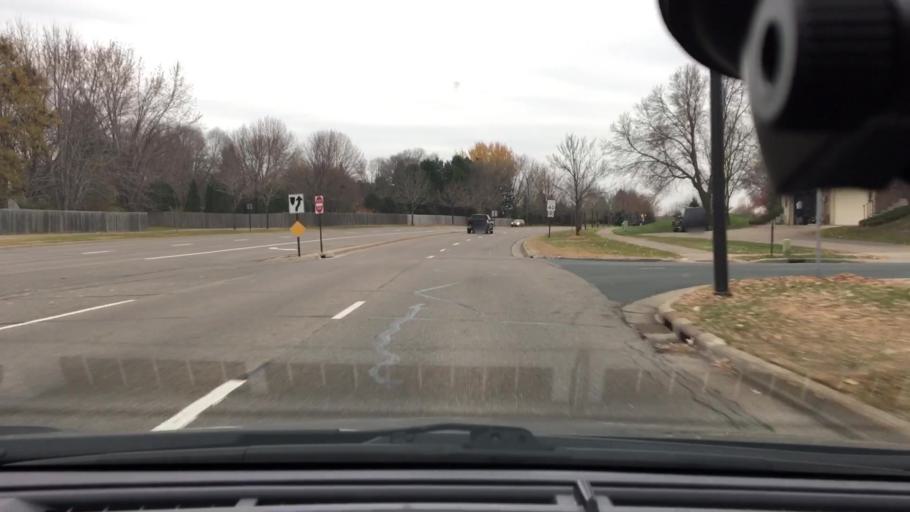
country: US
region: Minnesota
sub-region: Hennepin County
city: Maple Grove
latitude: 45.1112
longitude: -93.4514
